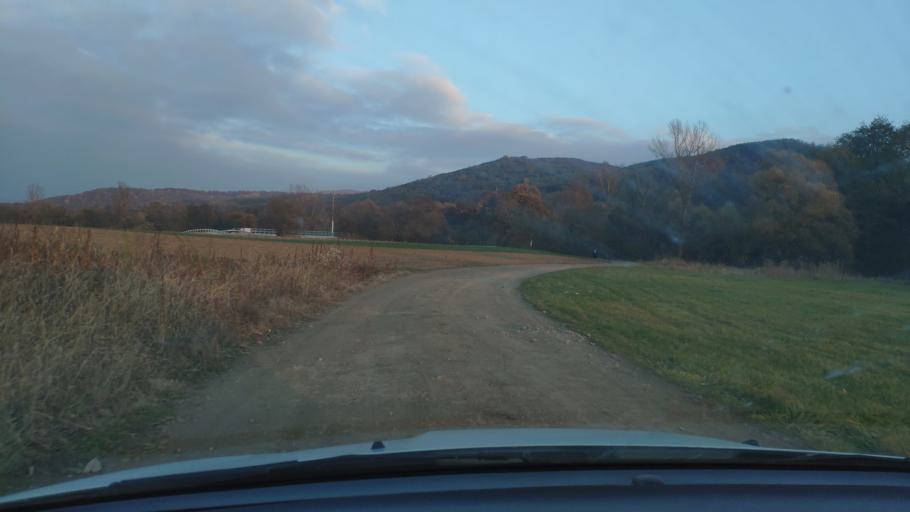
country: RO
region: Mures
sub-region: Comuna Chibed
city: Chibed
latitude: 46.5353
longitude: 24.9769
